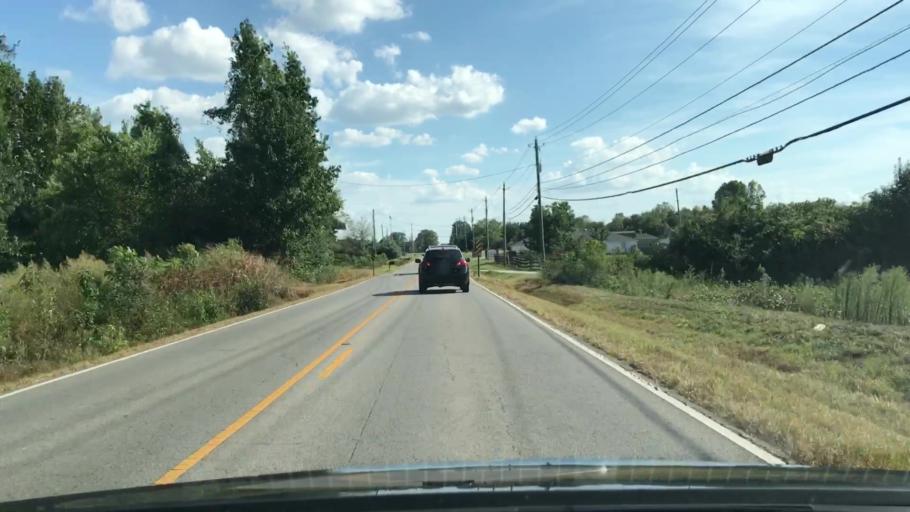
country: US
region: Alabama
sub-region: Madison County
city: Harvest
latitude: 34.8340
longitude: -86.7492
